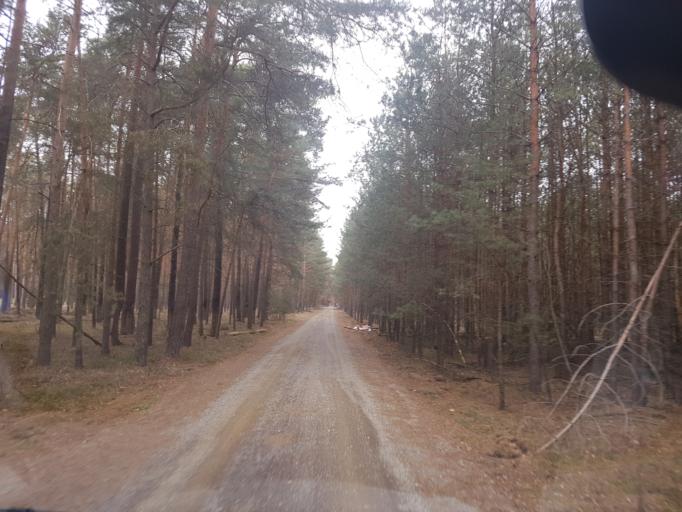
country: DE
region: Brandenburg
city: Hohenbucko
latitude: 51.7729
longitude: 13.4825
